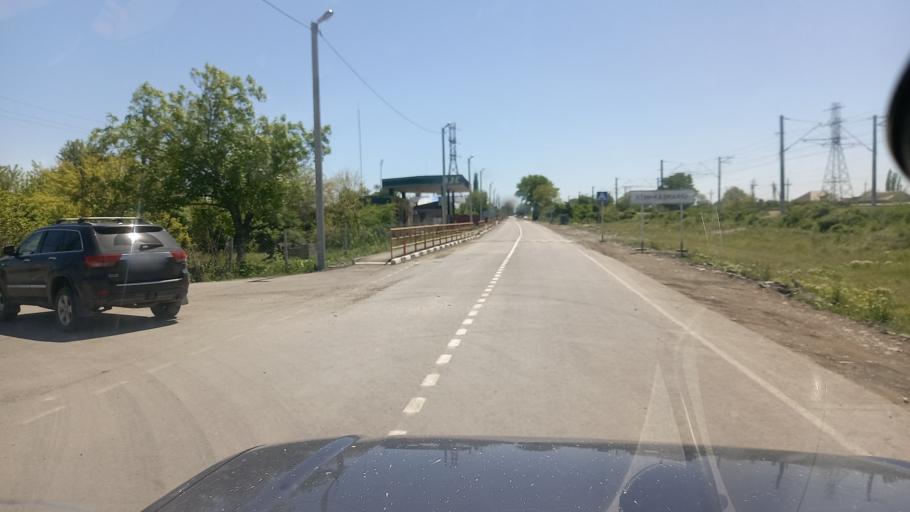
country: RU
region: Dagestan
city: Samur
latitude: 41.8083
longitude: 48.5159
